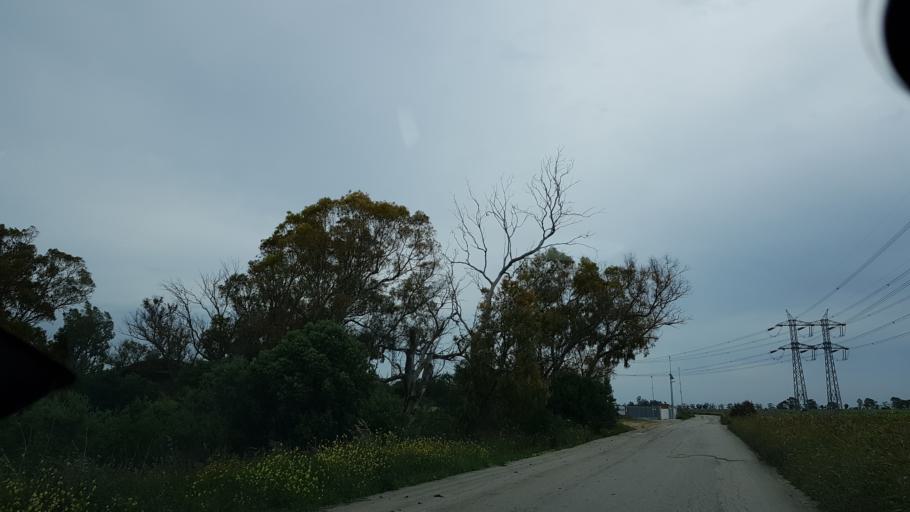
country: IT
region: Apulia
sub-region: Provincia di Brindisi
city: La Rosa
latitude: 40.6242
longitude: 17.9894
